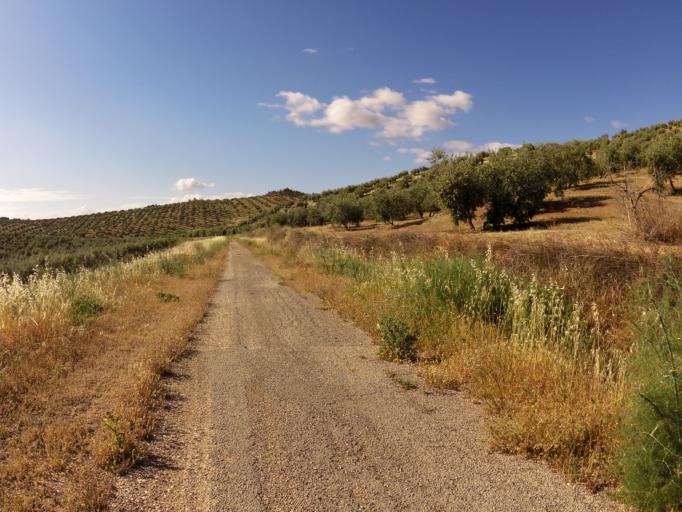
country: ES
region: Andalusia
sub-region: Province of Cordoba
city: Fuente-Tojar
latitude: 37.5810
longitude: -4.1856
